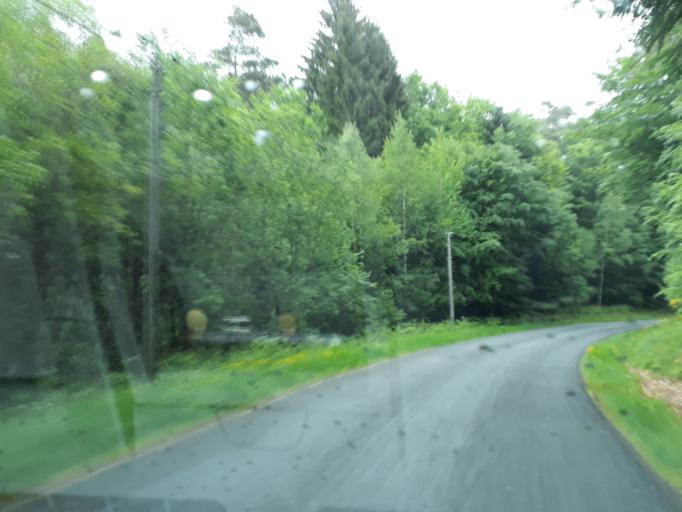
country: FR
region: Limousin
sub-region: Departement de la Haute-Vienne
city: Peyrat-le-Chateau
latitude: 45.8313
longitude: 1.8485
